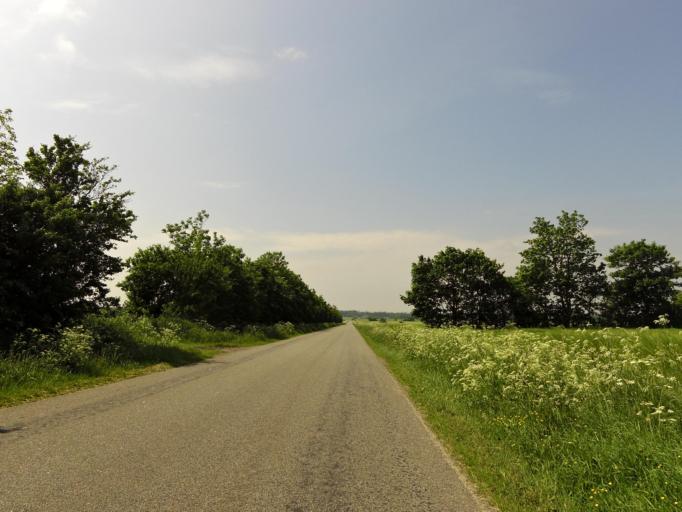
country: DK
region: South Denmark
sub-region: Tonder Kommune
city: Toftlund
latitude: 55.1913
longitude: 9.0024
